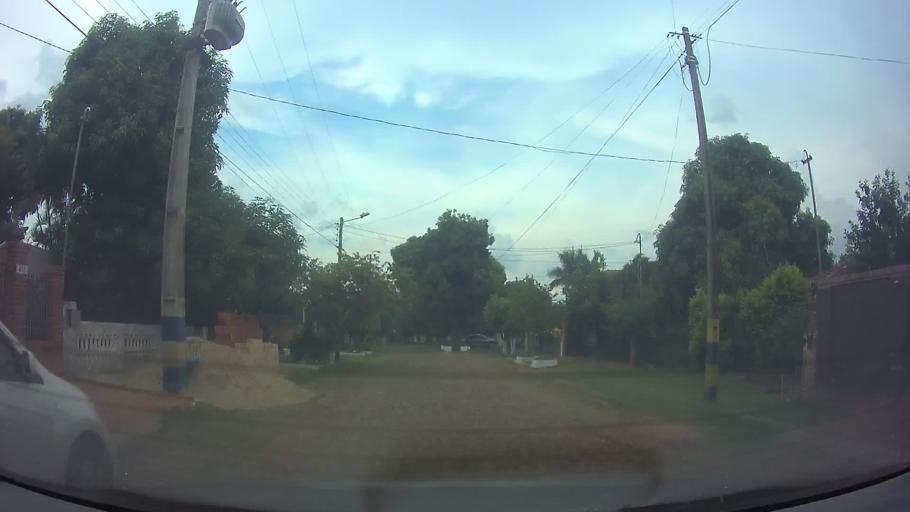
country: PY
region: Central
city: San Lorenzo
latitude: -25.2824
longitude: -57.4937
